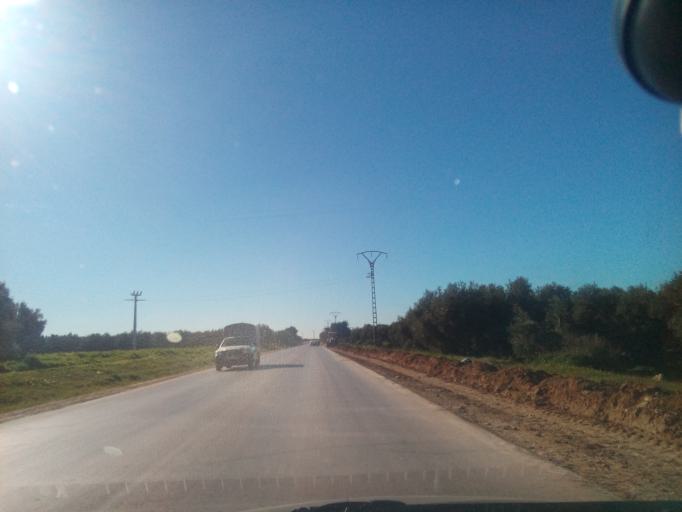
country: DZ
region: Relizane
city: Djidiouia
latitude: 35.9203
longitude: 0.7944
